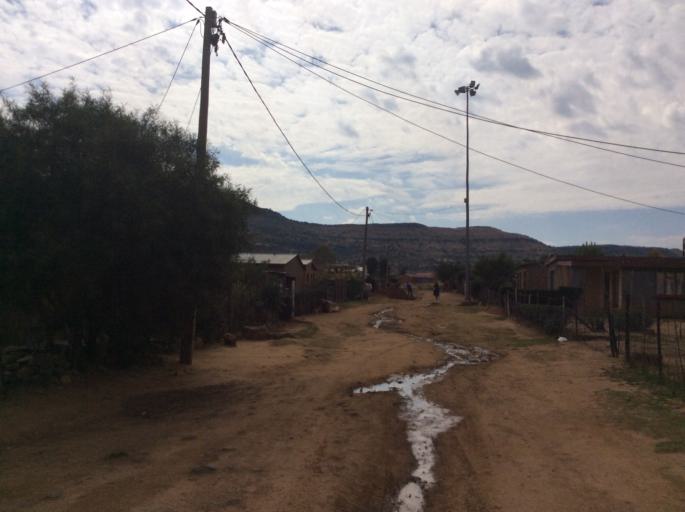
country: LS
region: Mafeteng
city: Mafeteng
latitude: -29.7214
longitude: 27.0247
